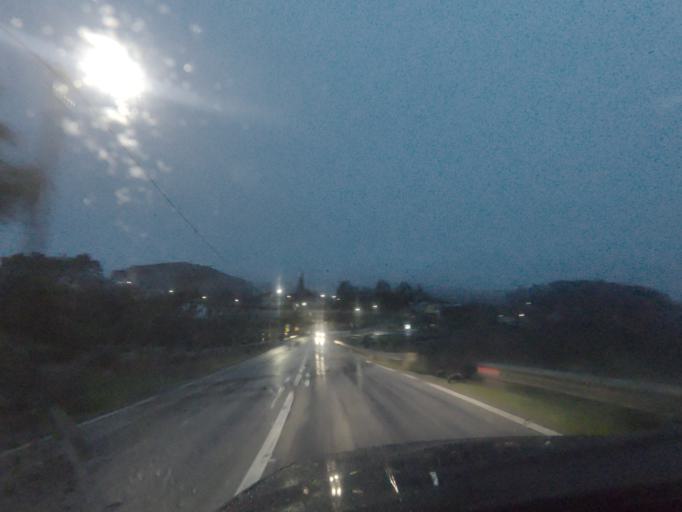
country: PT
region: Vila Real
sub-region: Vila Real
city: Vila Real
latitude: 41.2911
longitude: -7.7060
